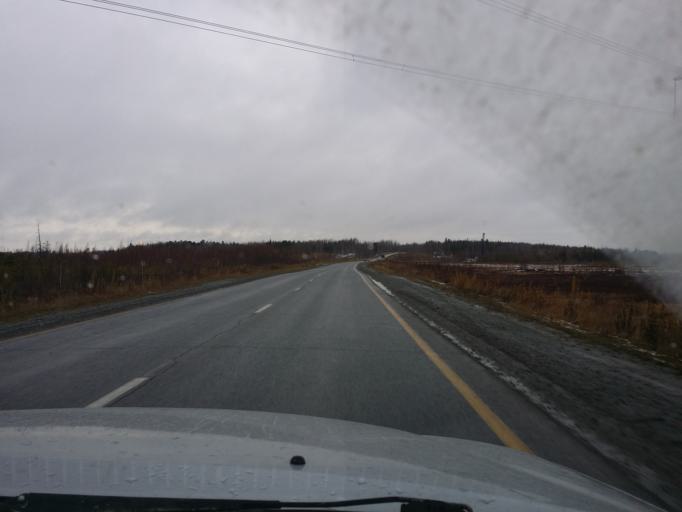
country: RU
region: Khanty-Mansiyskiy Avtonomnyy Okrug
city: Megion
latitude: 61.1069
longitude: 76.0080
